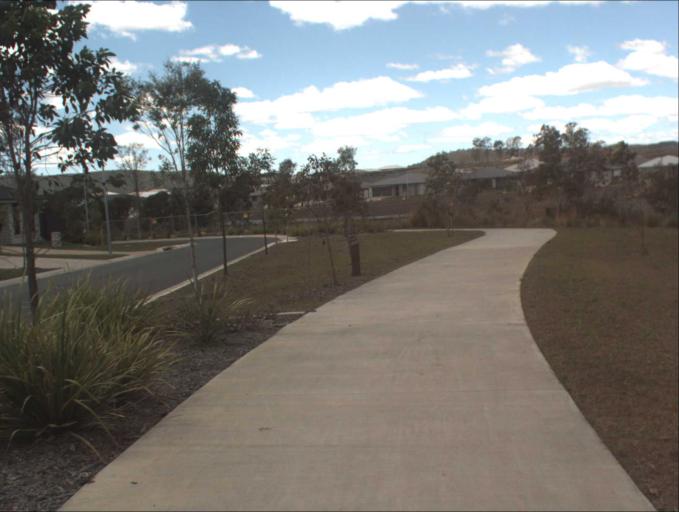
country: AU
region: Queensland
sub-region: Logan
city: Chambers Flat
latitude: -27.8027
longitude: 153.1104
